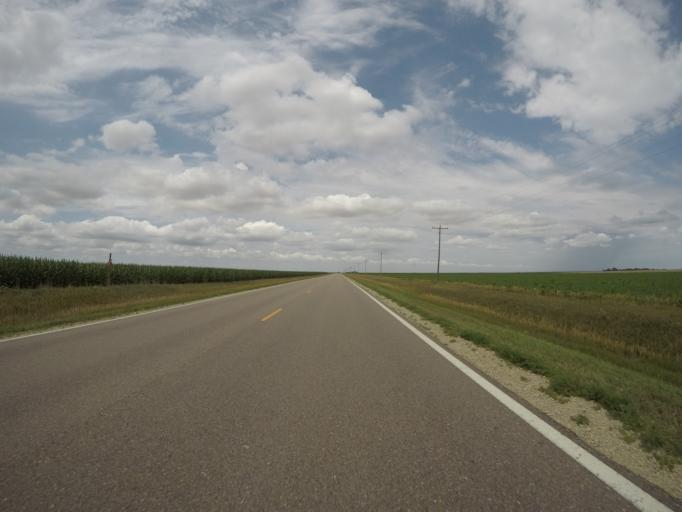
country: US
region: Kansas
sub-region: Rawlins County
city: Atwood
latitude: 39.6584
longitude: -101.0569
